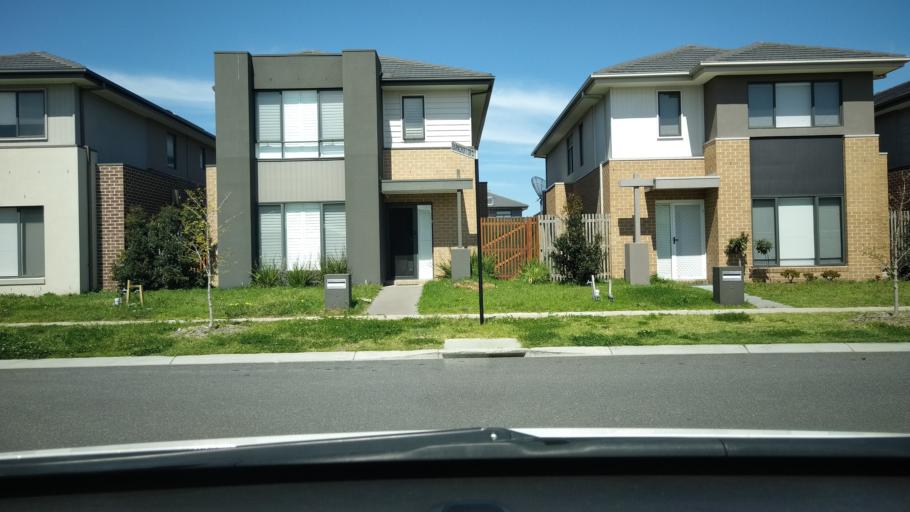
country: AU
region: Victoria
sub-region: Greater Dandenong
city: Keysborough
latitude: -38.0009
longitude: 145.1727
